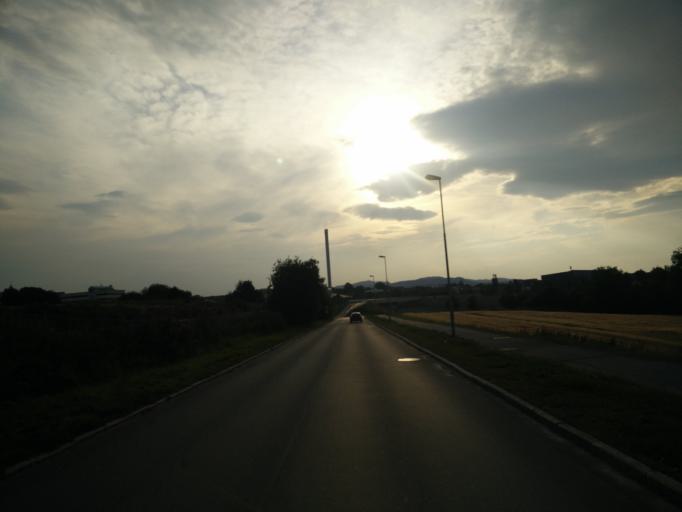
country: NO
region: Sor-Trondelag
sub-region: Trondheim
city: Trondheim
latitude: 63.4367
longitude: 10.4777
